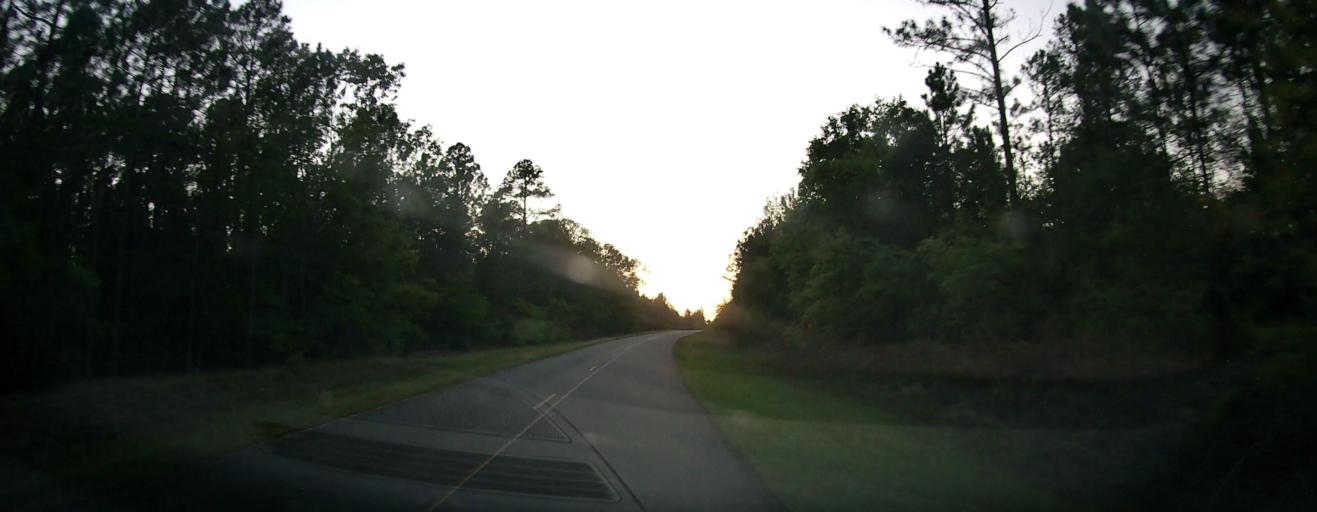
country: US
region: Georgia
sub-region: Marion County
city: Buena Vista
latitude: 32.2544
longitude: -84.6179
